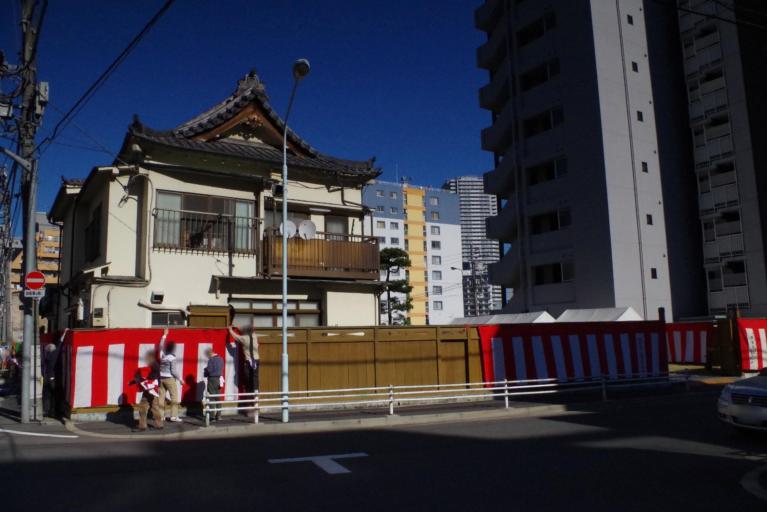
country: JP
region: Tokyo
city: Tokyo
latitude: 35.6703
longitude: 139.7804
